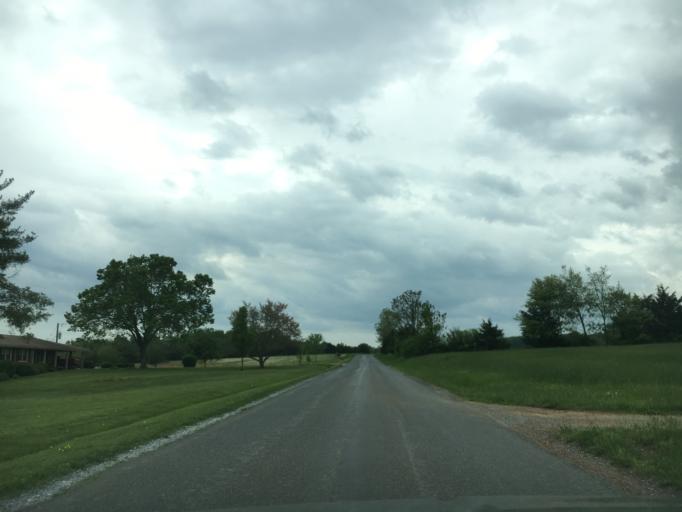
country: US
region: Virginia
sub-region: Campbell County
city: Rustburg
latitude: 37.1767
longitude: -79.0437
